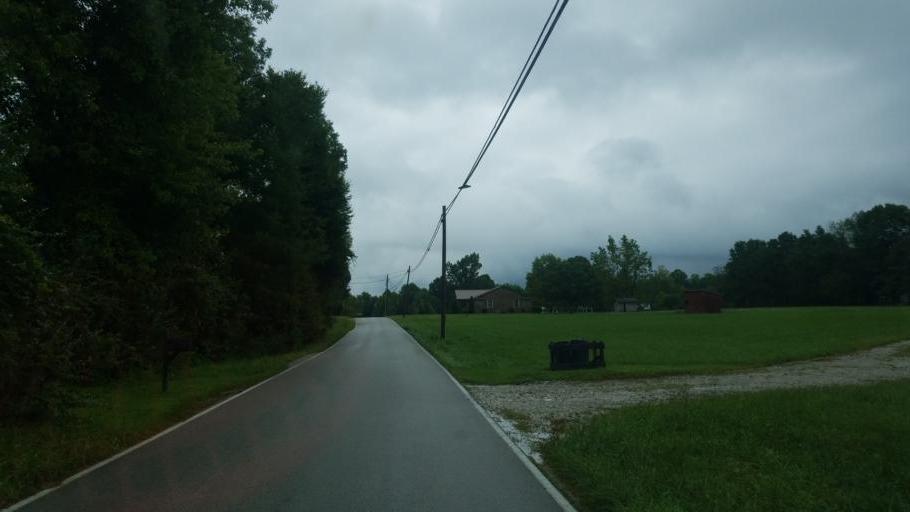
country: US
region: Kentucky
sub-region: Rowan County
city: Morehead
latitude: 38.1584
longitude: -83.5061
